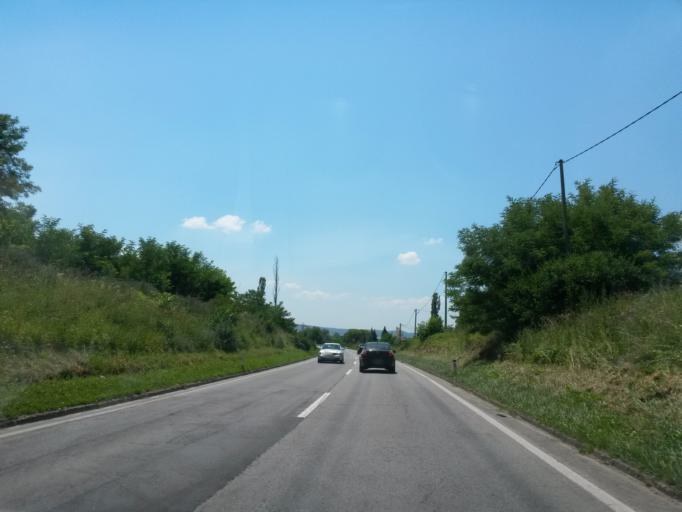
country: BA
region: Republika Srpska
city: Doboj
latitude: 44.8153
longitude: 18.0522
